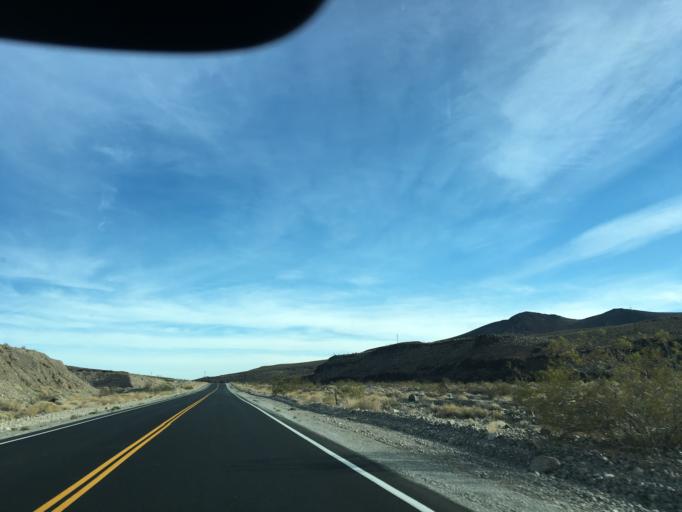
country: US
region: Nevada
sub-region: Nye County
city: Beatty
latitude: 36.3591
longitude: -116.6496
